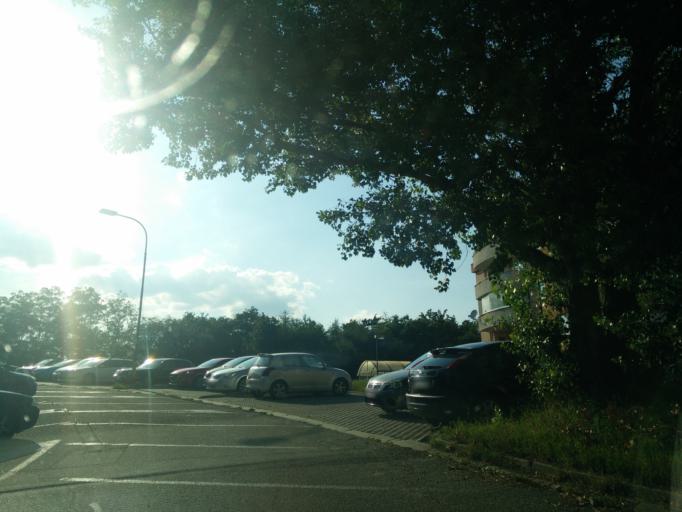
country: AT
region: Lower Austria
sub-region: Politischer Bezirk Bruck an der Leitha
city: Wolfsthal
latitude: 48.1953
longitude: 17.0250
